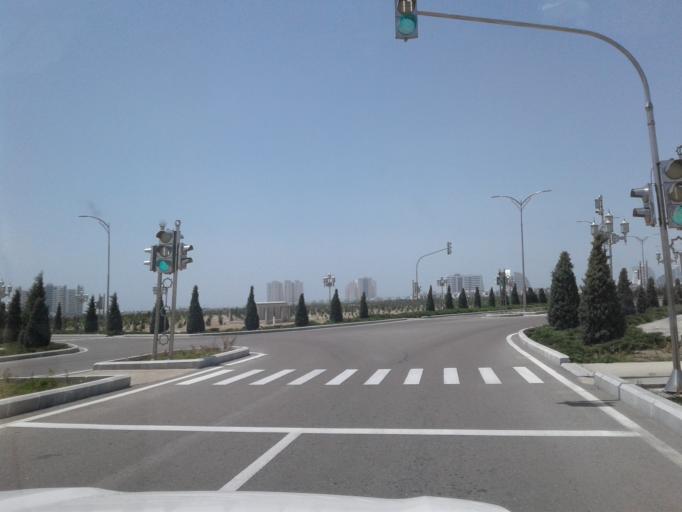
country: TM
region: Balkan
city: Turkmenbasy
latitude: 39.9681
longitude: 52.8448
